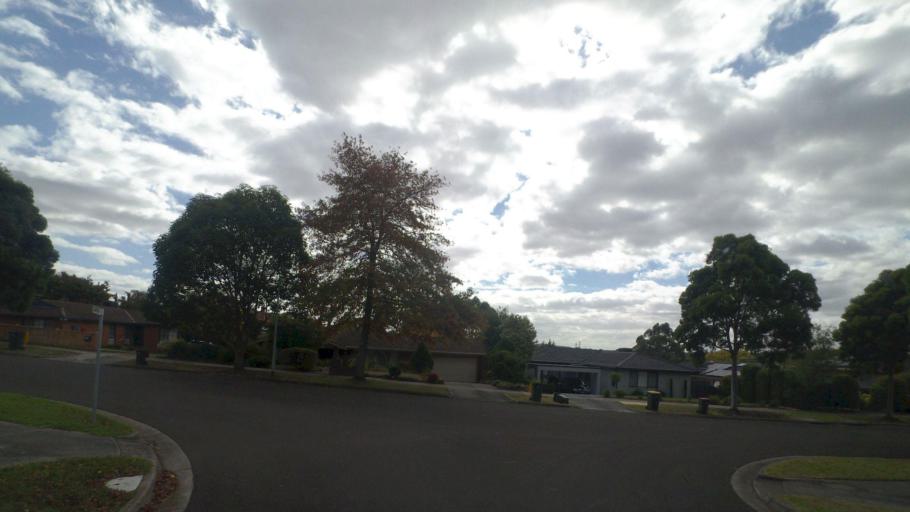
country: AU
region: Victoria
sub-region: Manningham
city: Donvale
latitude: -37.7598
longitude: 145.1764
